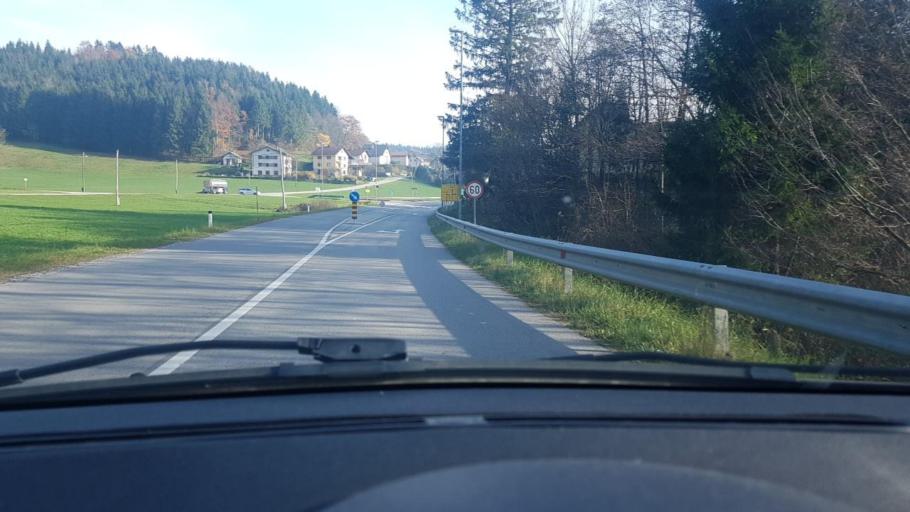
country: SI
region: Kranj
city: Golnik
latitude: 46.3219
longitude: 14.3404
